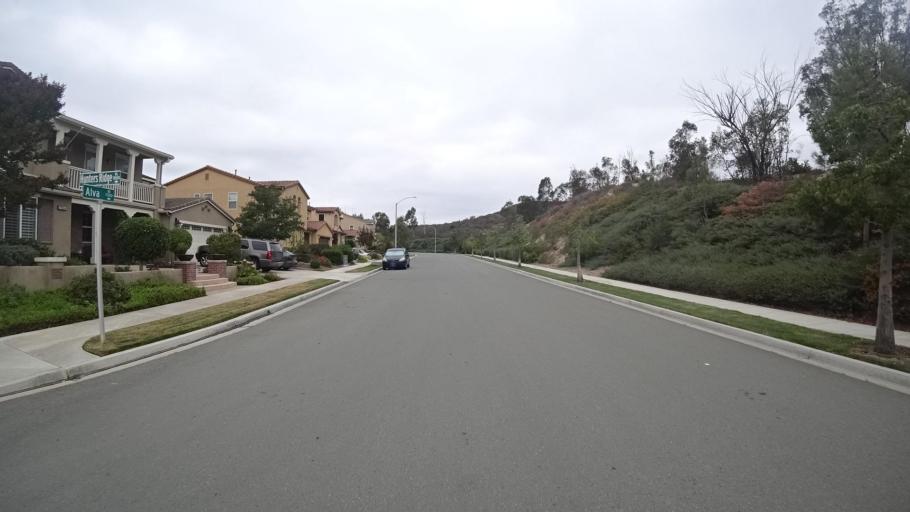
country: US
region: California
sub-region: San Diego County
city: Escondido
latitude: 33.0389
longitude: -117.1119
